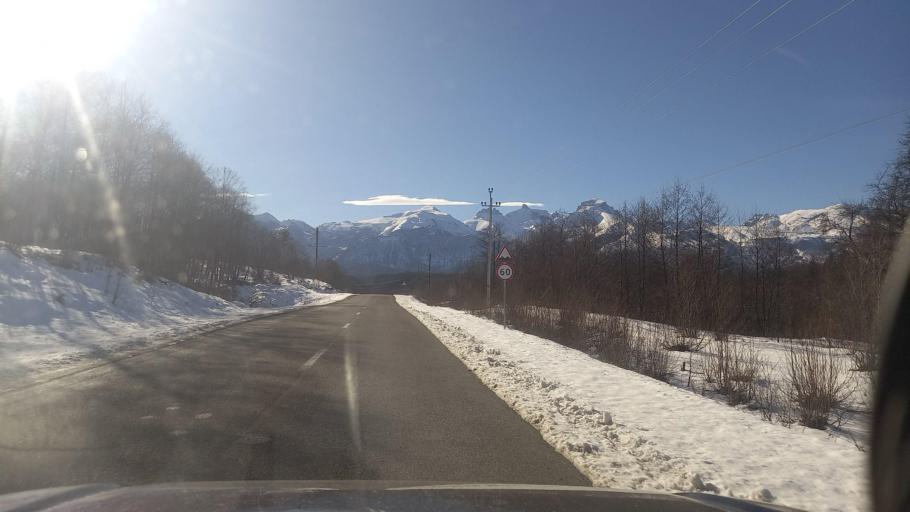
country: RU
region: North Ossetia
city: Chikola
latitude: 43.1248
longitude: 43.8169
